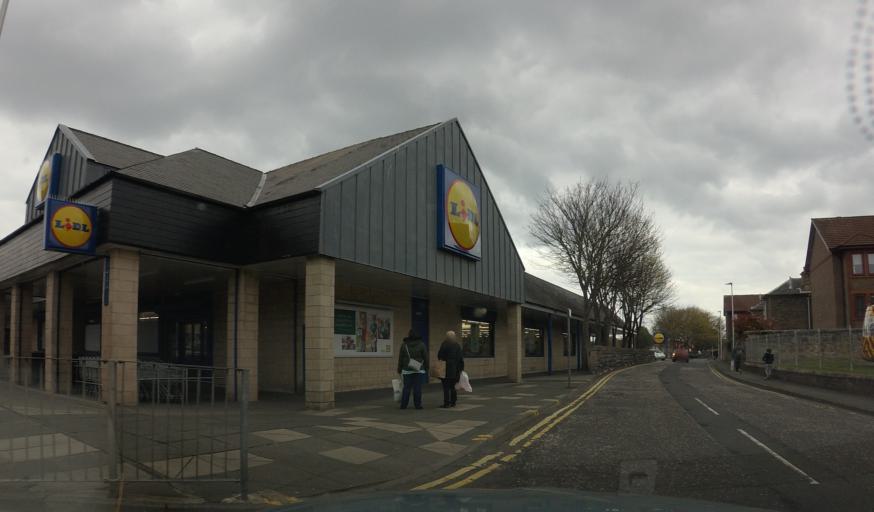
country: GB
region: Scotland
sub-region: Midlothian
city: Dalkeith
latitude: 55.8913
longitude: -3.0706
